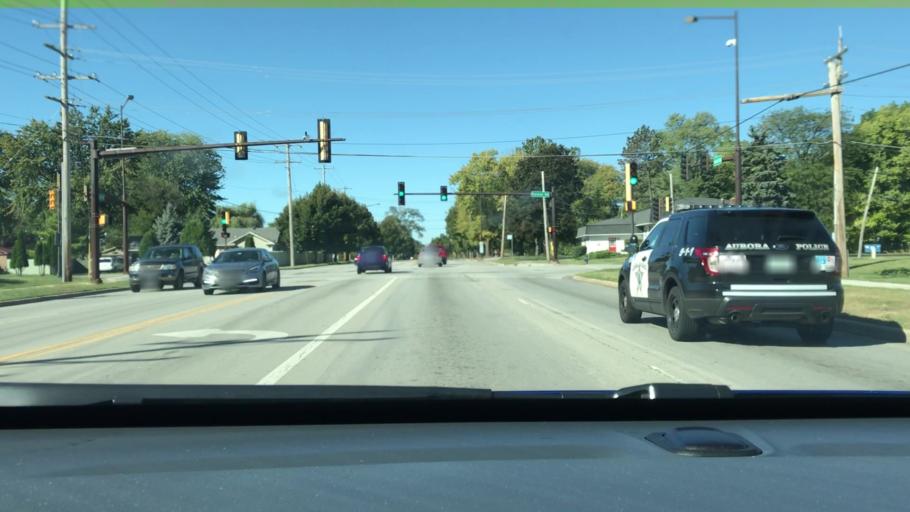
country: US
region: Illinois
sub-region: Kane County
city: North Aurora
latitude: 41.7811
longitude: -88.3491
